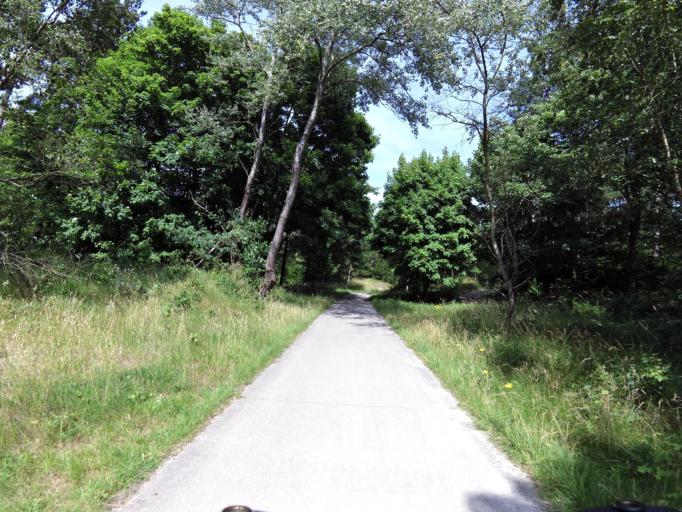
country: NL
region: Zeeland
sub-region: Schouwen-Duiveland
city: Burgh
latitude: 51.6846
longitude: 3.6961
